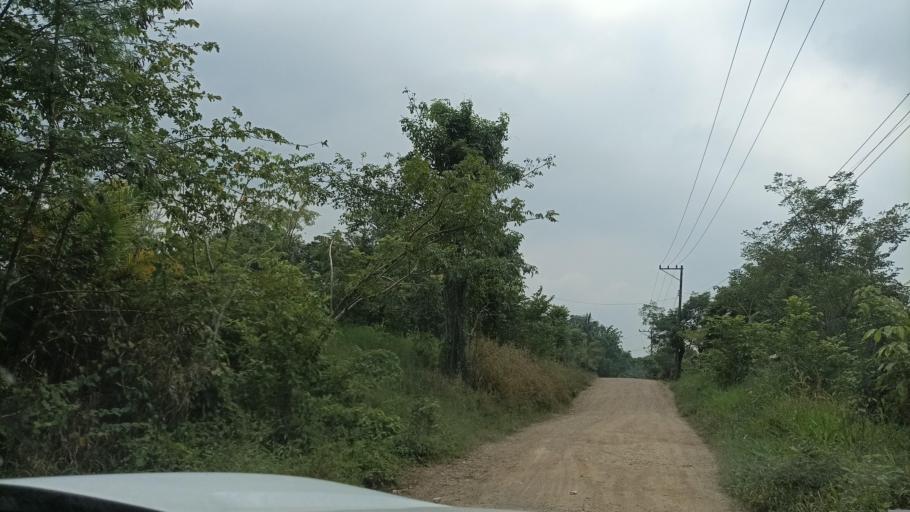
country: MX
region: Veracruz
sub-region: Moloacan
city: Cuichapa
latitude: 17.5818
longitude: -94.2337
